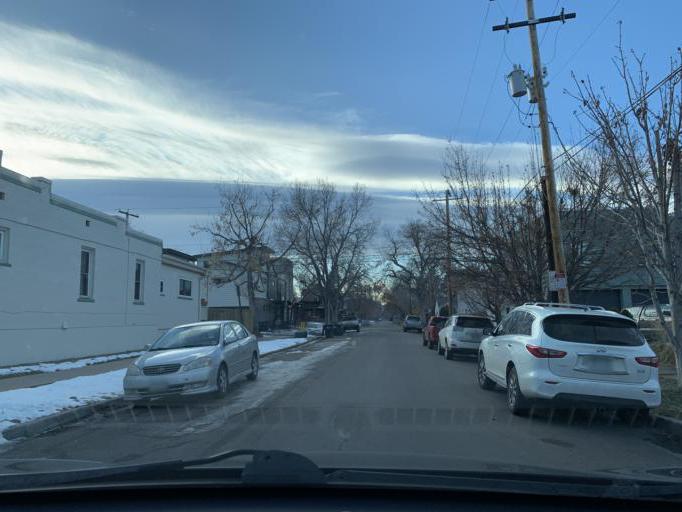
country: US
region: Colorado
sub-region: Jefferson County
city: Edgewater
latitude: 39.7711
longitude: -105.0452
